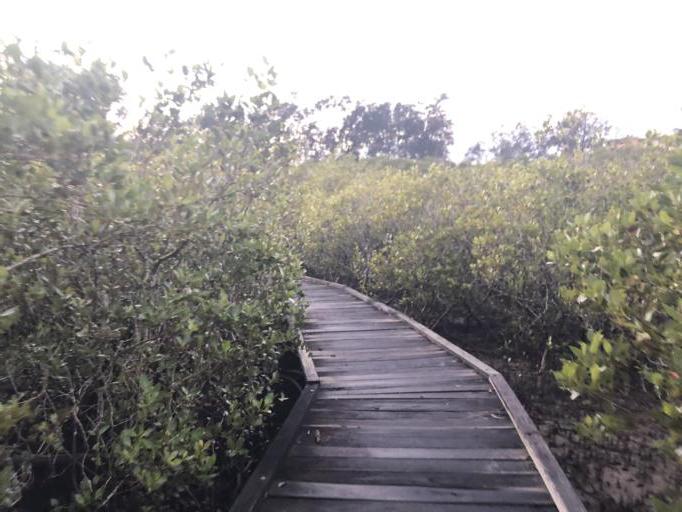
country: AU
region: New South Wales
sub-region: Coffs Harbour
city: Coffs Harbour
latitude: -30.3009
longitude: 153.1334
